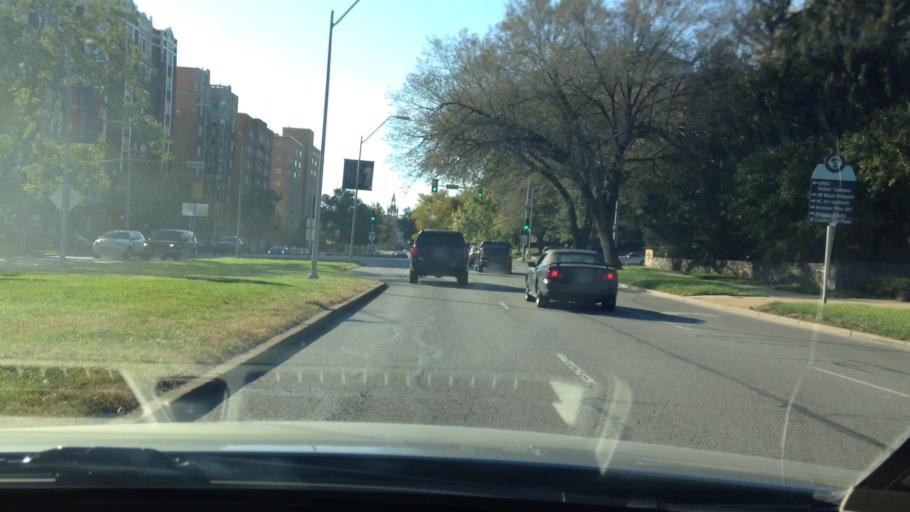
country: US
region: Kansas
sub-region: Johnson County
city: Westwood
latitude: 39.0421
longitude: -94.5814
